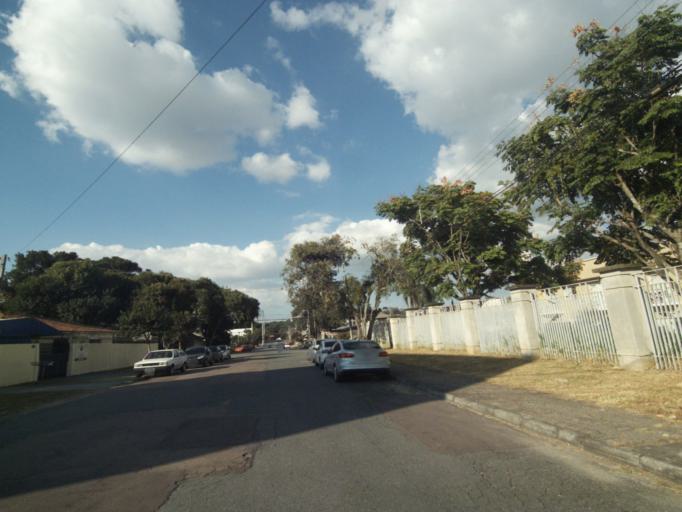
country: BR
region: Parana
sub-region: Curitiba
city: Curitiba
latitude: -25.4577
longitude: -49.2536
